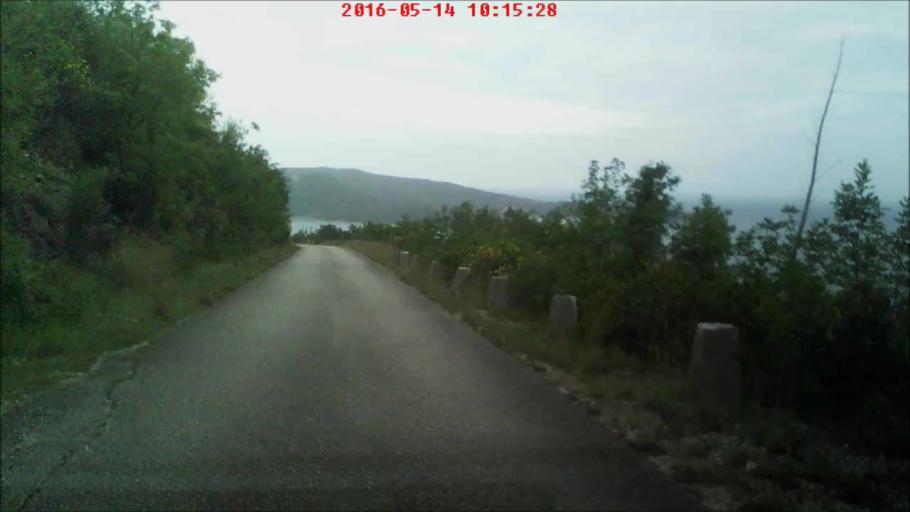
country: HR
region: Dubrovacko-Neretvanska
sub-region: Grad Dubrovnik
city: Mokosica
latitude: 42.7304
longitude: 17.9635
